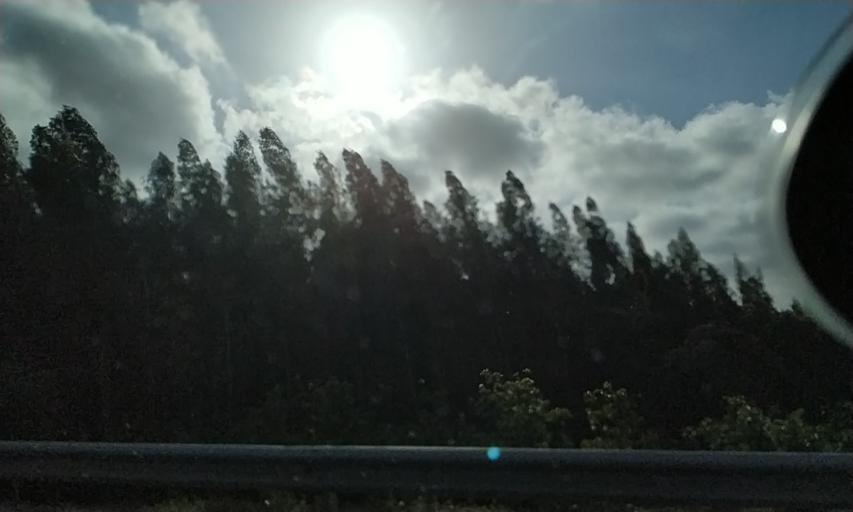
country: PT
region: Leiria
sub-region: Bombarral
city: Bombarral
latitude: 39.2419
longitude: -9.1701
